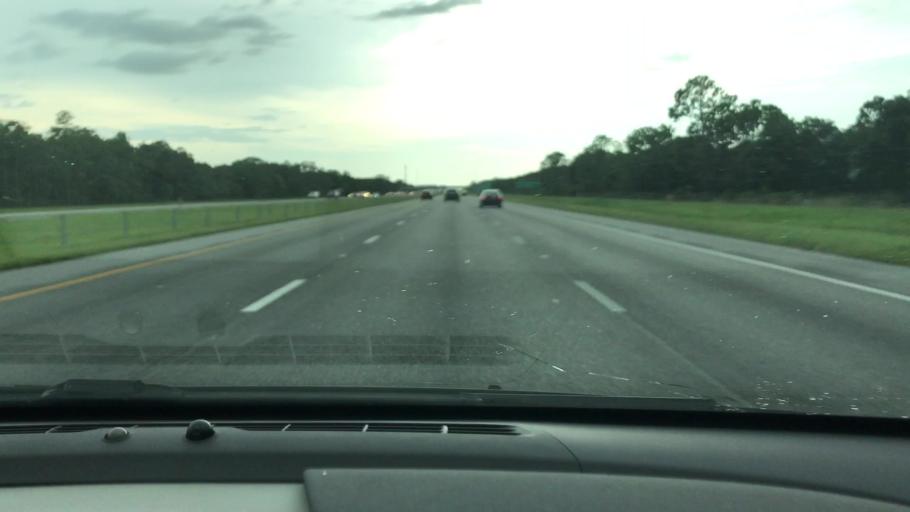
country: US
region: Florida
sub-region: Sarasota County
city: Plantation
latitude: 27.1125
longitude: -82.3293
